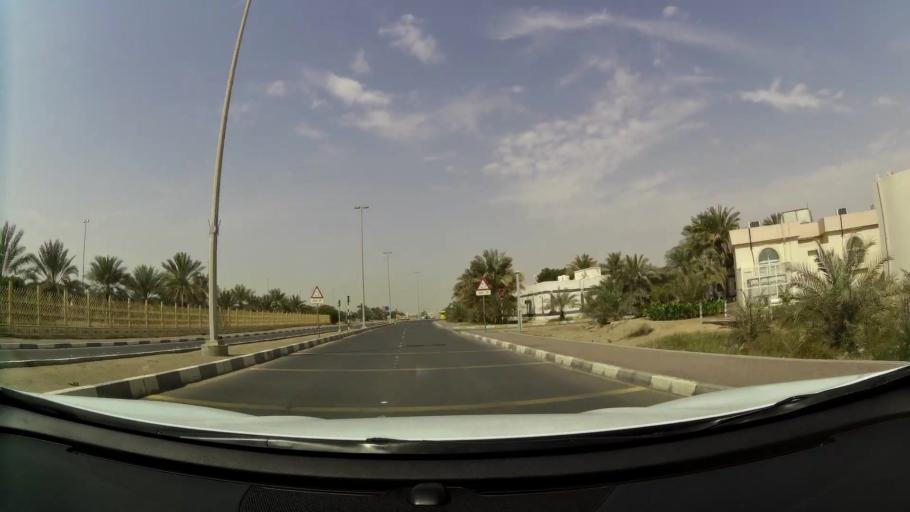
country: AE
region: Abu Dhabi
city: Abu Dhabi
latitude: 24.2948
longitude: 54.6308
